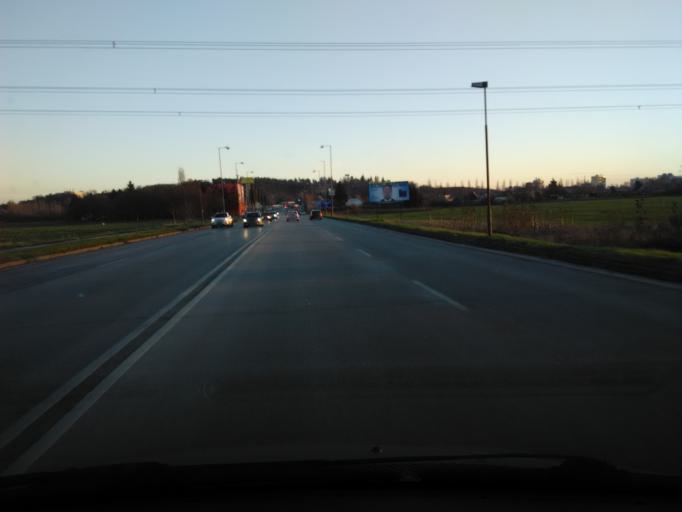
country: SK
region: Nitriansky
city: Levice
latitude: 48.2320
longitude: 18.6008
